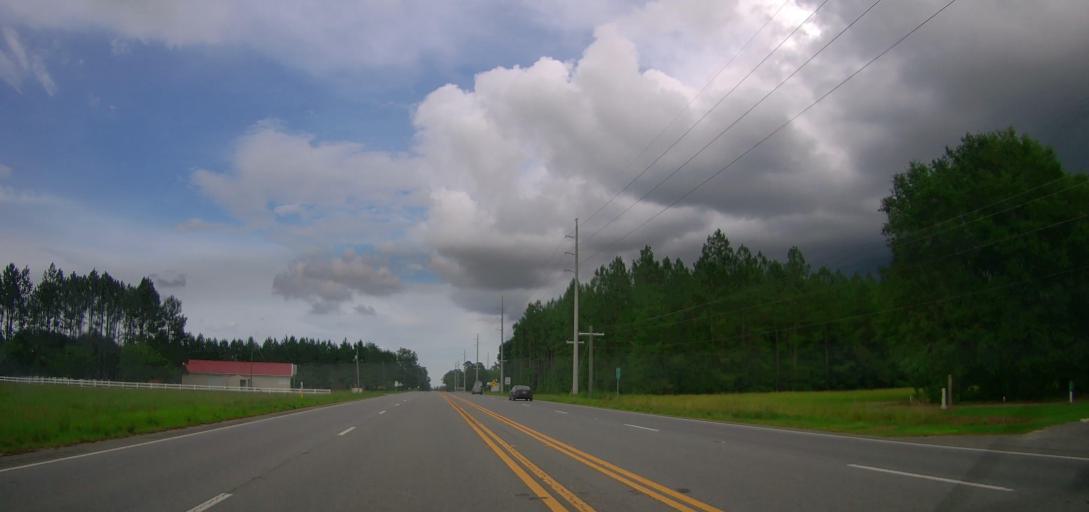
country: US
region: Georgia
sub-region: Pierce County
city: Blackshear
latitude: 31.4057
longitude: -82.1169
